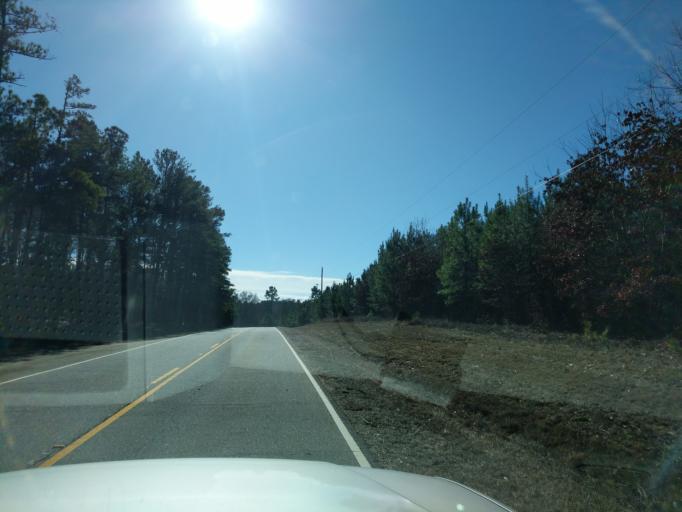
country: US
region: South Carolina
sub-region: Saluda County
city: Saluda
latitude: 34.0965
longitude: -81.8293
